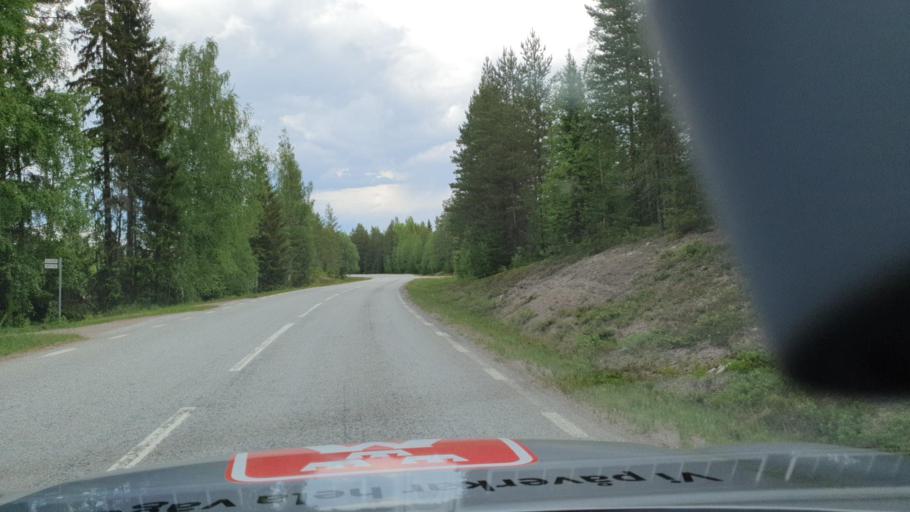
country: SE
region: Vaesterbotten
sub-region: Asele Kommun
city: Asele
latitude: 63.8346
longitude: 17.1583
